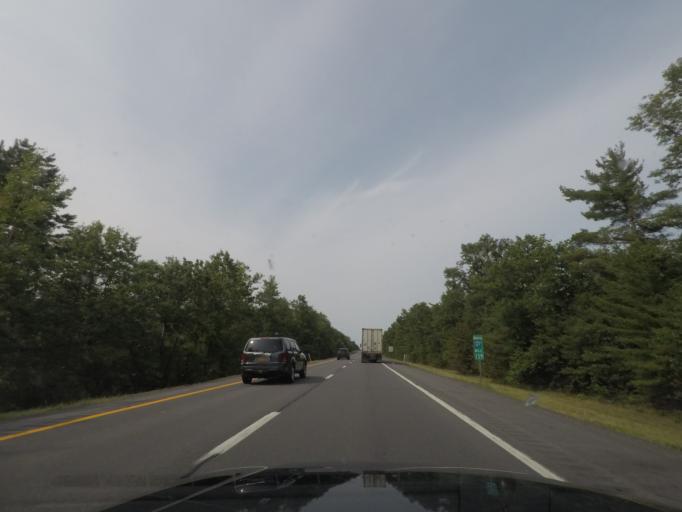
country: US
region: New York
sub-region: Essex County
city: Keeseville
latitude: 44.5014
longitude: -73.5007
